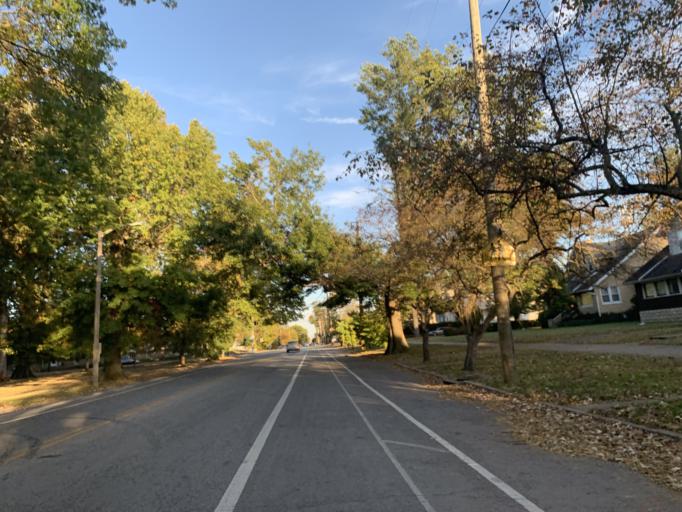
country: US
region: Indiana
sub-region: Floyd County
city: New Albany
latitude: 38.2505
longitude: -85.8281
